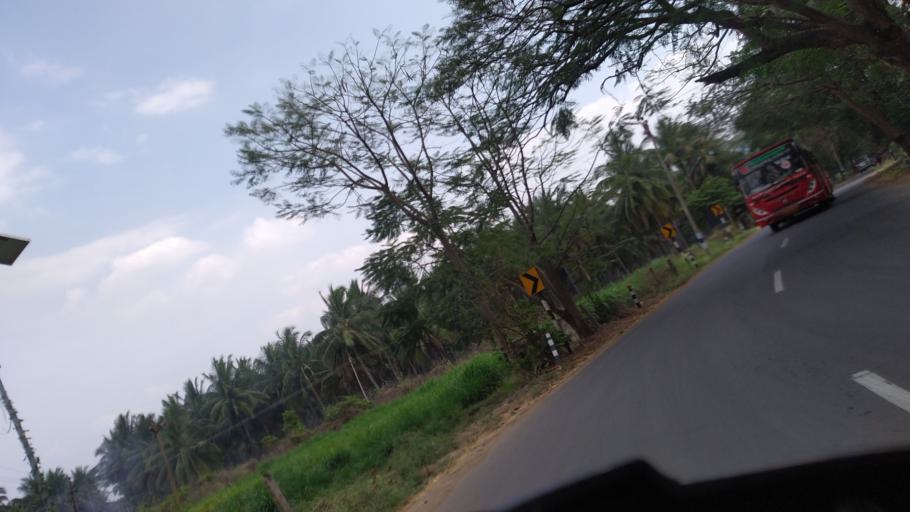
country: IN
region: Tamil Nadu
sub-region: Coimbatore
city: Perur
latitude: 10.9617
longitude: 76.7494
